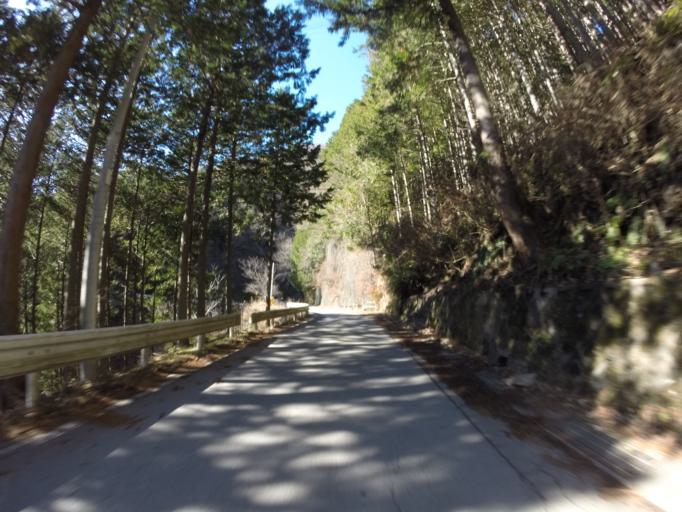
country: JP
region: Yamanashi
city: Ryuo
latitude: 35.4117
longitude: 138.3360
